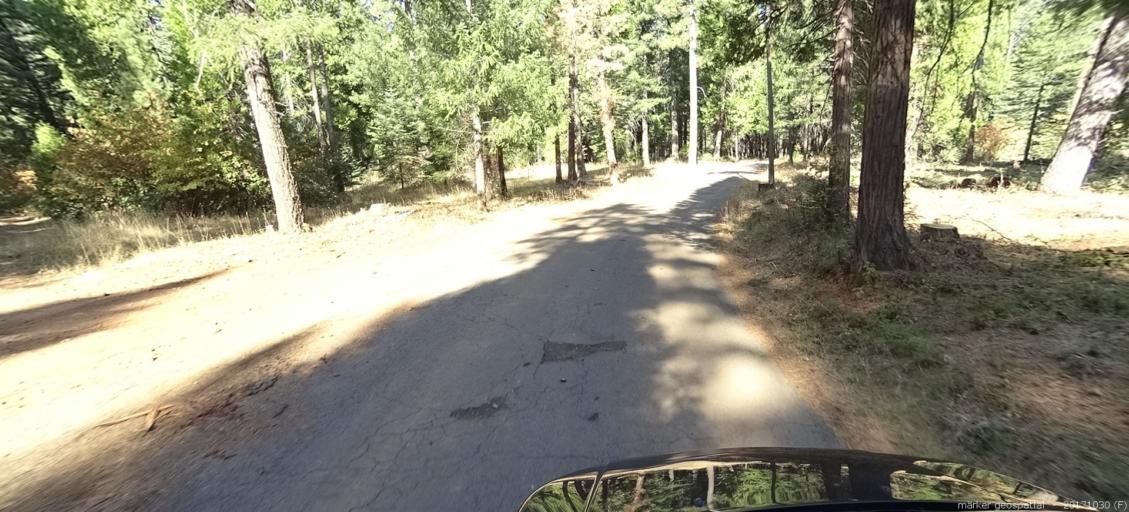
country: US
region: California
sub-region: Shasta County
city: Shingletown
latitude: 40.5158
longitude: -121.9014
